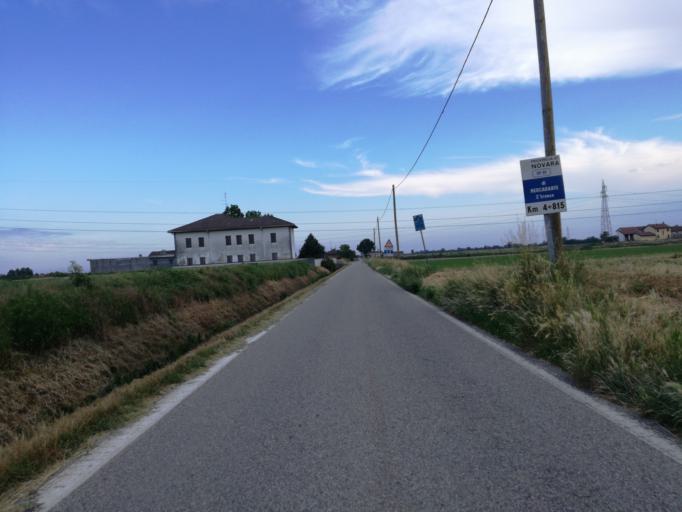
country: IT
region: Piedmont
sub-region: Provincia di Novara
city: Torrion Quartara
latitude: 45.4160
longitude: 8.6191
